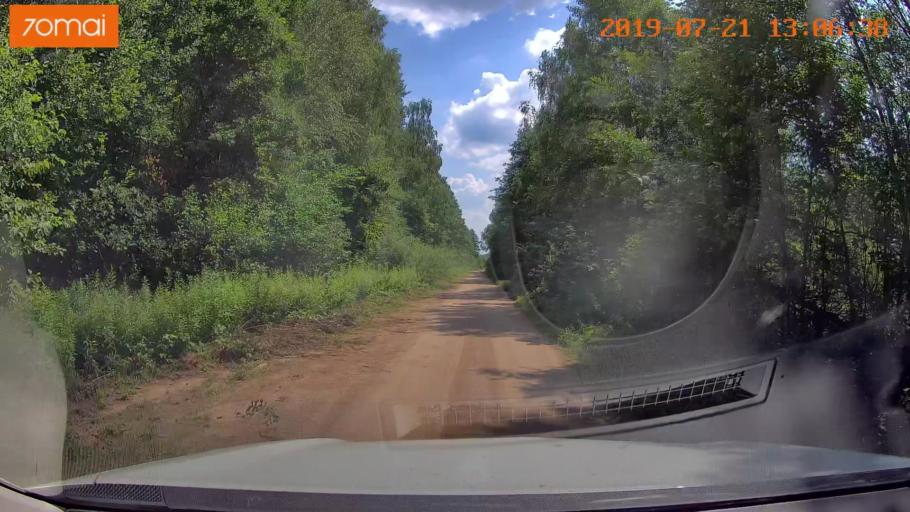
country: BY
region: Grodnenskaya
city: Lyubcha
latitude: 53.8288
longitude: 26.0426
